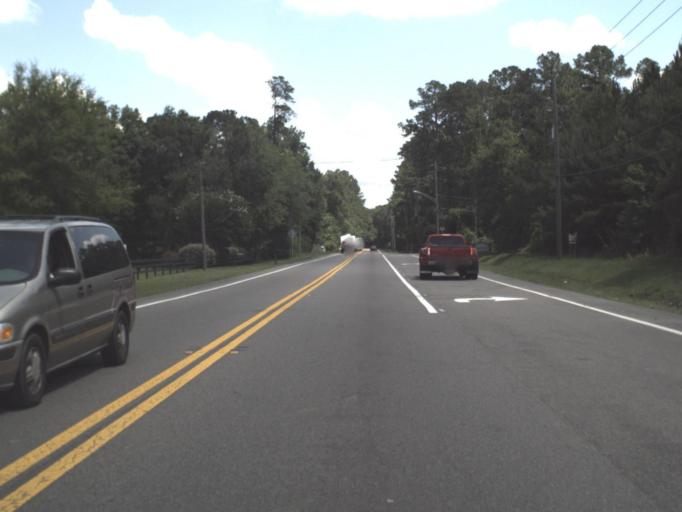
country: US
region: Florida
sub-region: Nassau County
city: Nassau Village-Ratliff
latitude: 30.4610
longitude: -81.7068
